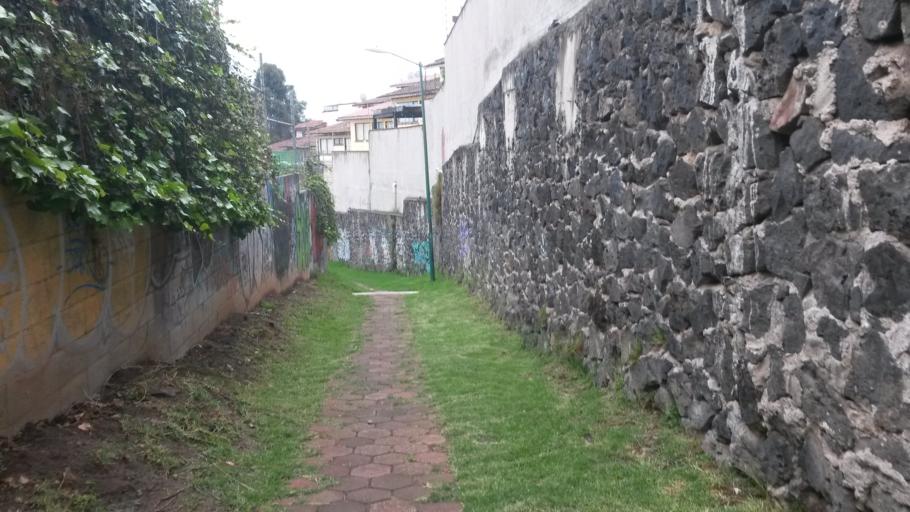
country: MX
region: Mexico City
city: Magdalena Contreras
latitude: 19.3008
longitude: -99.2390
